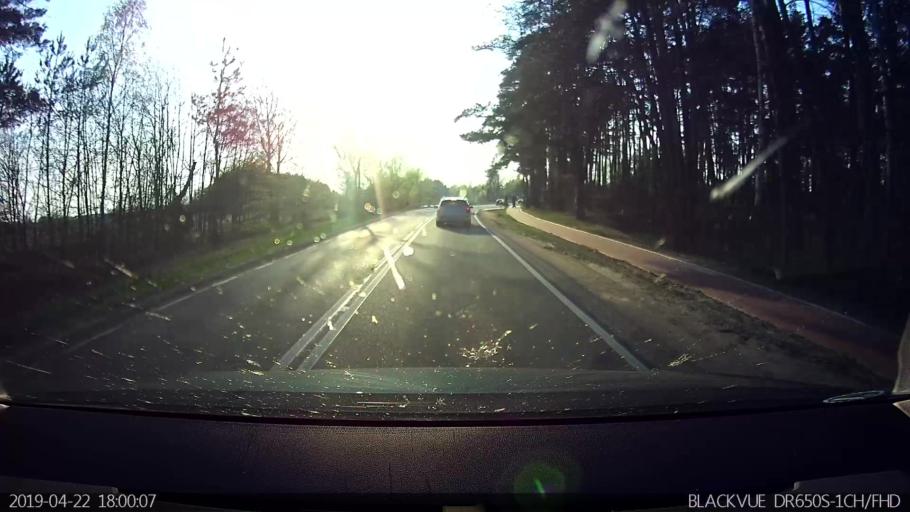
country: PL
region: Masovian Voivodeship
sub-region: Powiat wegrowski
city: Korytnica
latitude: 52.4753
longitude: 21.8509
